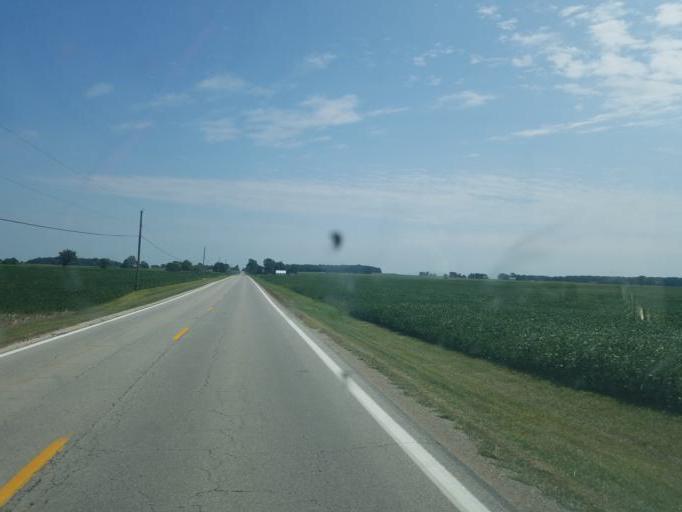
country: US
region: Ohio
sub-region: Marion County
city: Marion
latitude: 40.6877
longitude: -83.1839
